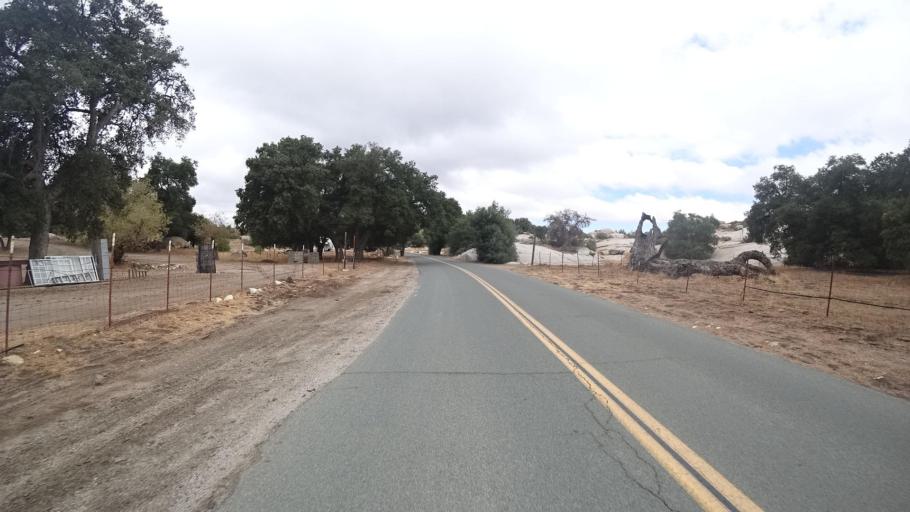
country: US
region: California
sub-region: San Diego County
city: Campo
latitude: 32.6238
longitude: -116.3226
